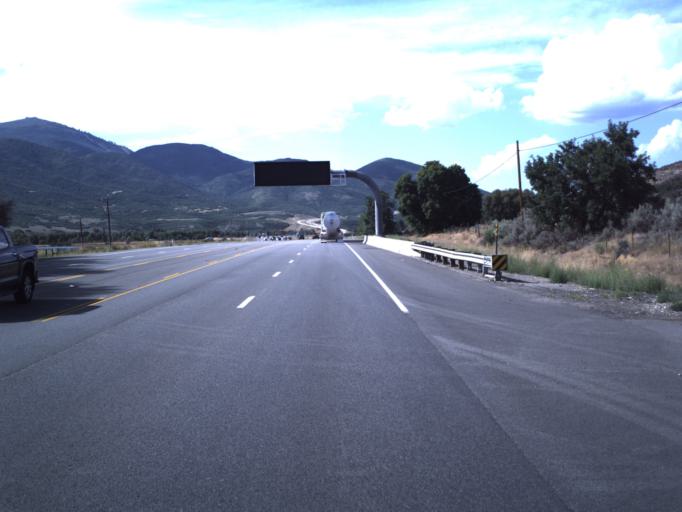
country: US
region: Utah
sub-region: Wasatch County
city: Heber
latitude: 40.5514
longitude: -111.4221
